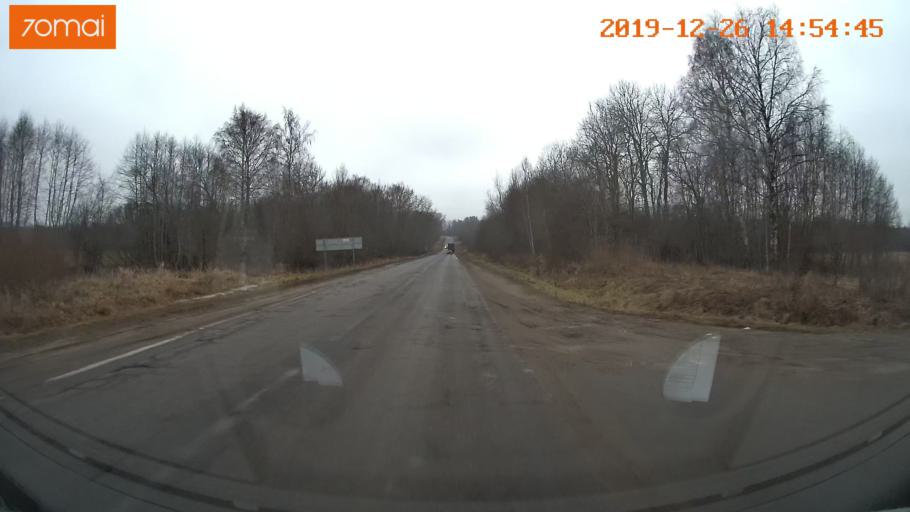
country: RU
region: Jaroslavl
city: Rybinsk
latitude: 58.3054
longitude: 38.8817
